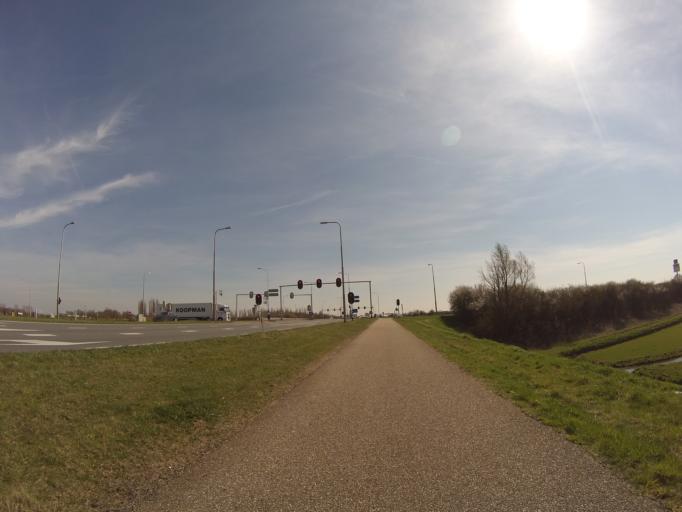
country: NL
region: Gelderland
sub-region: Gemeente Nijkerk
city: Nijkerk
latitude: 52.2449
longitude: 5.4795
